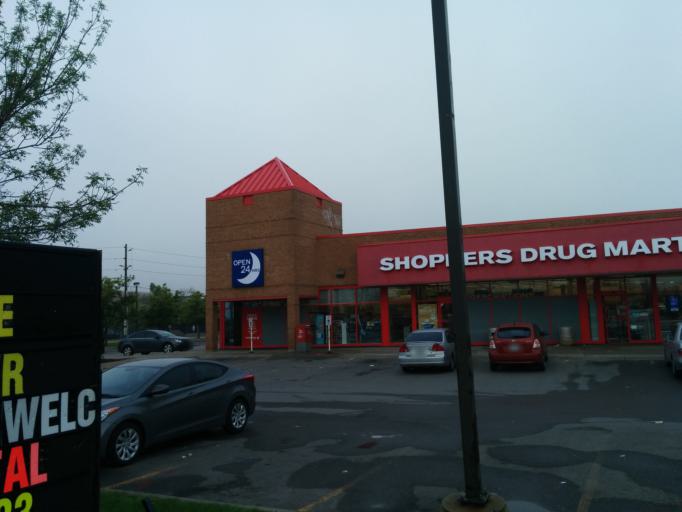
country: CA
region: Ontario
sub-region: York
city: Richmond Hill
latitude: 43.8874
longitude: -79.4412
